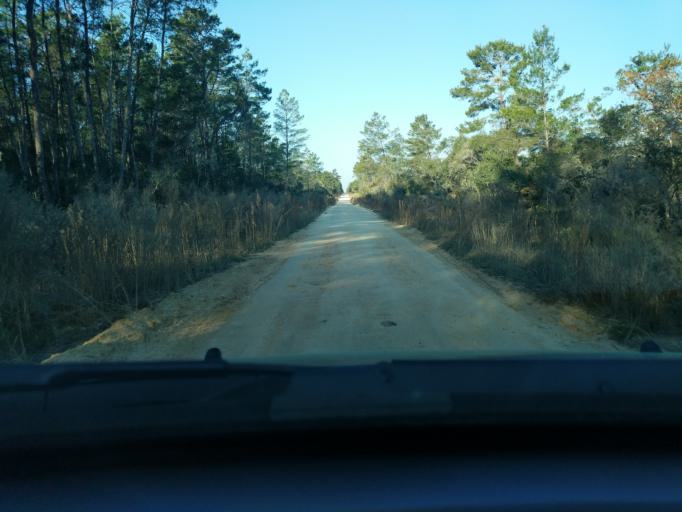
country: US
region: Florida
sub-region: Lake County
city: Astor
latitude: 29.2259
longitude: -81.7434
